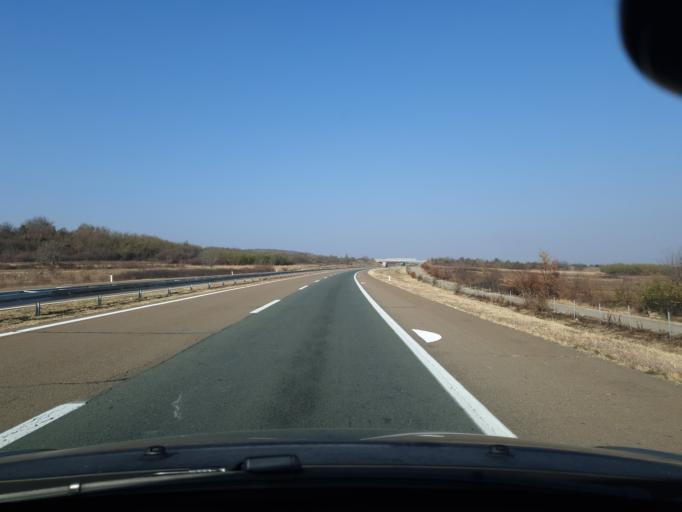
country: RS
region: Central Serbia
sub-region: Nisavski Okrug
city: Doljevac
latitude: 43.2388
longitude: 21.8189
